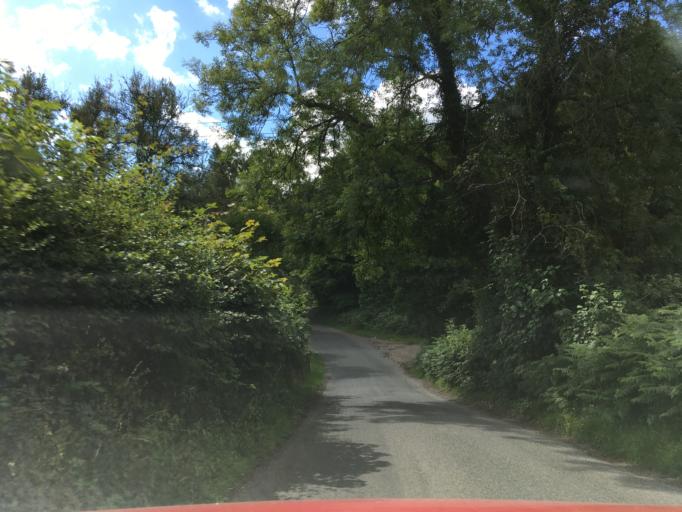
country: GB
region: England
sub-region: Gloucestershire
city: Bream
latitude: 51.7431
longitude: -2.5579
